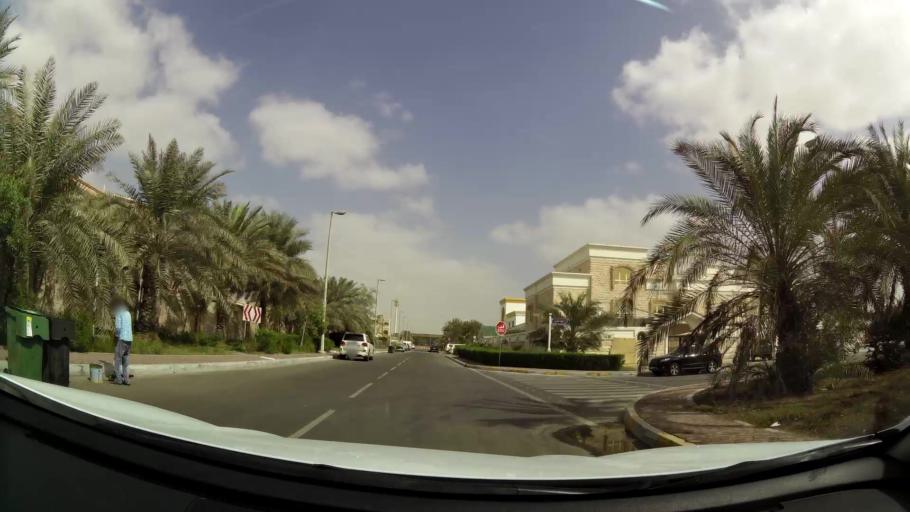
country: AE
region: Abu Dhabi
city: Abu Dhabi
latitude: 24.4111
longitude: 54.4984
